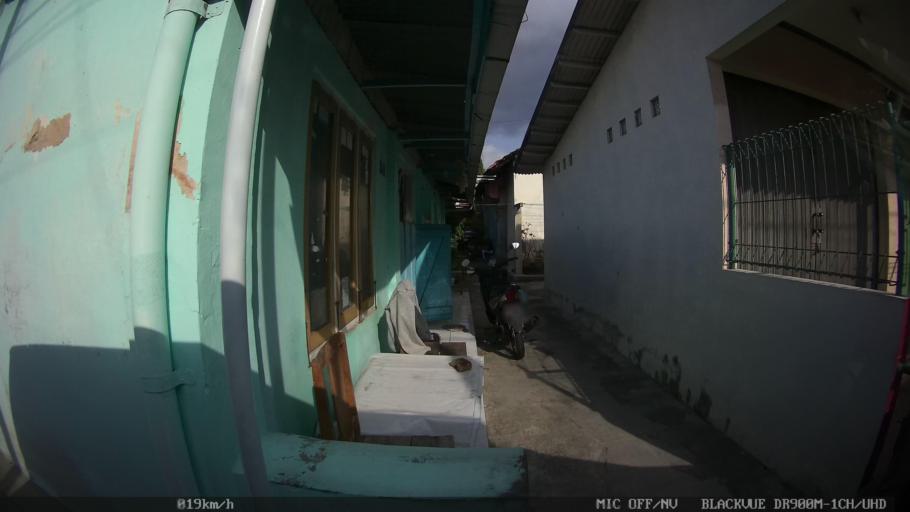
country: ID
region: Daerah Istimewa Yogyakarta
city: Yogyakarta
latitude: -7.8149
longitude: 110.3592
